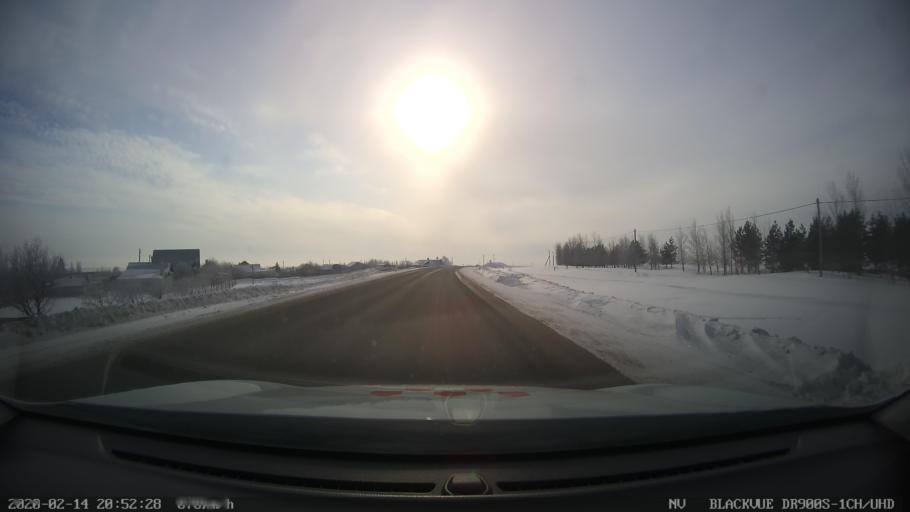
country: RU
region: Tatarstan
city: Kuybyshevskiy Zaton
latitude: 55.2040
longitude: 49.2492
